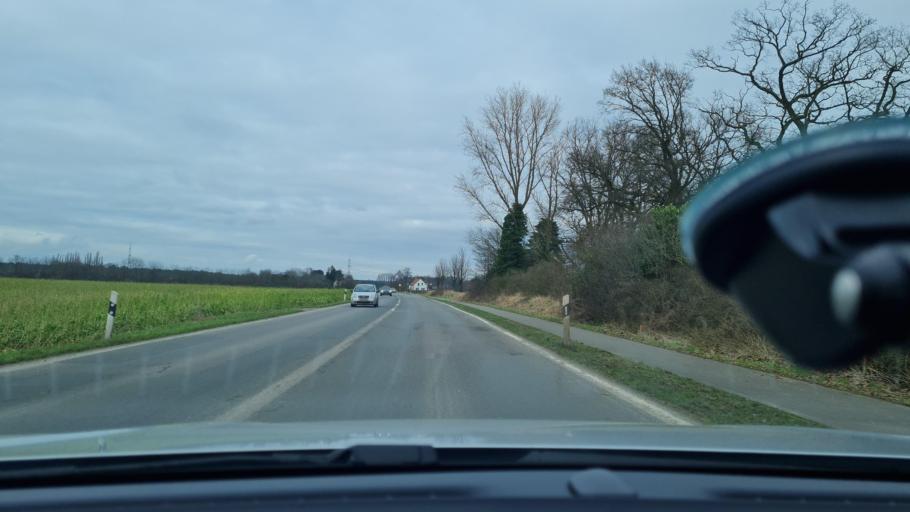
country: DE
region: North Rhine-Westphalia
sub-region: Regierungsbezirk Dusseldorf
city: Voerde
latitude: 51.6088
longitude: 6.6804
